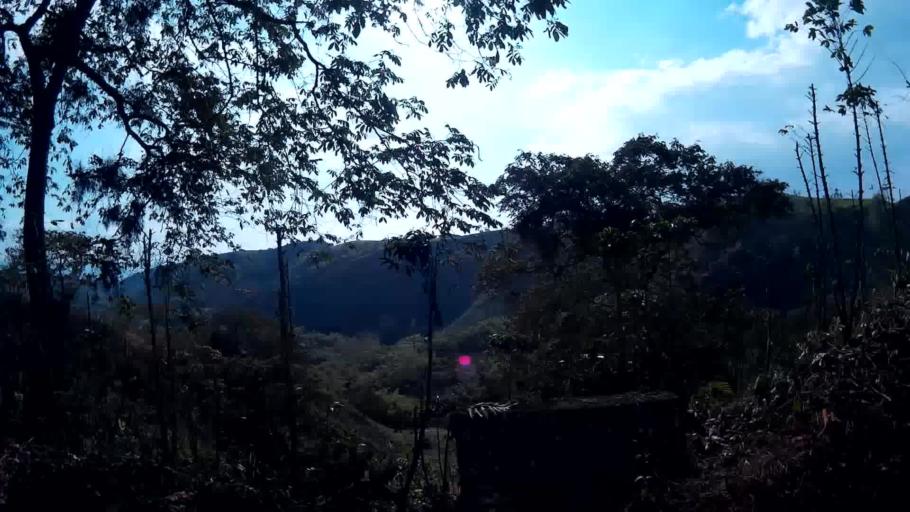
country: CO
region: Valle del Cauca
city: Ulloa
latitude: 4.7153
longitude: -75.7063
